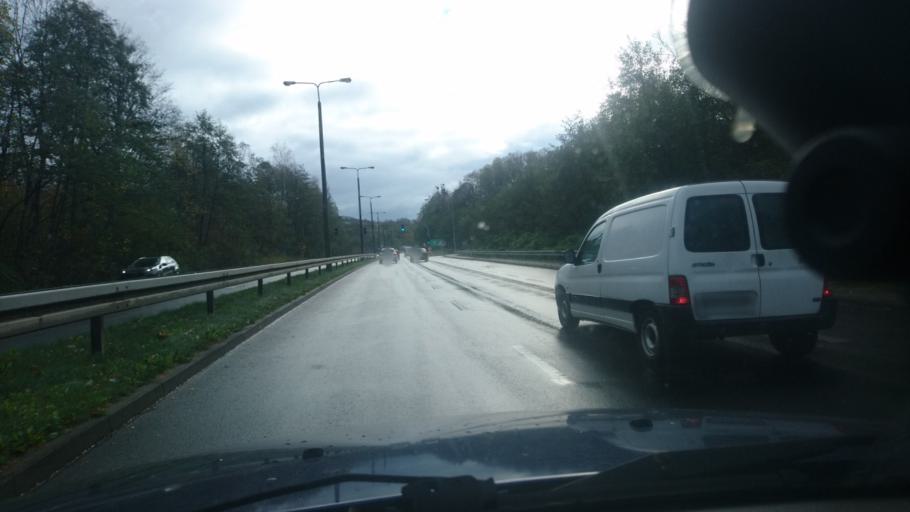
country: PL
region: Silesian Voivodeship
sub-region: Powiat bielski
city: Mazancowice
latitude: 49.8392
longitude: 19.0052
